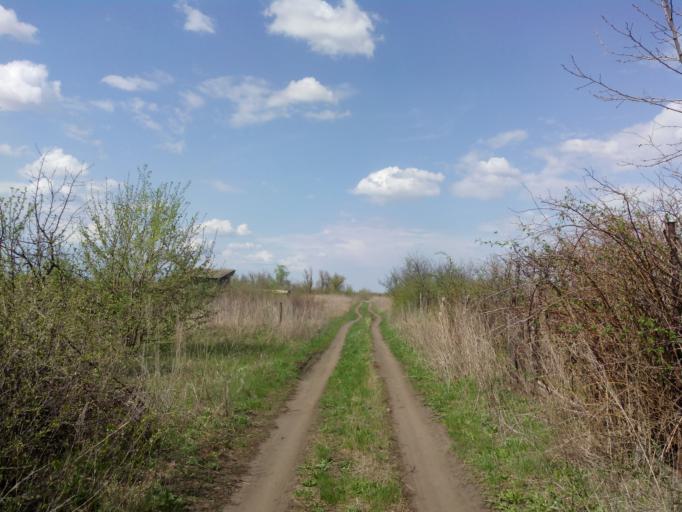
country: RU
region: Voronezj
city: Borisoglebsk
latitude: 51.3764
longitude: 42.1488
